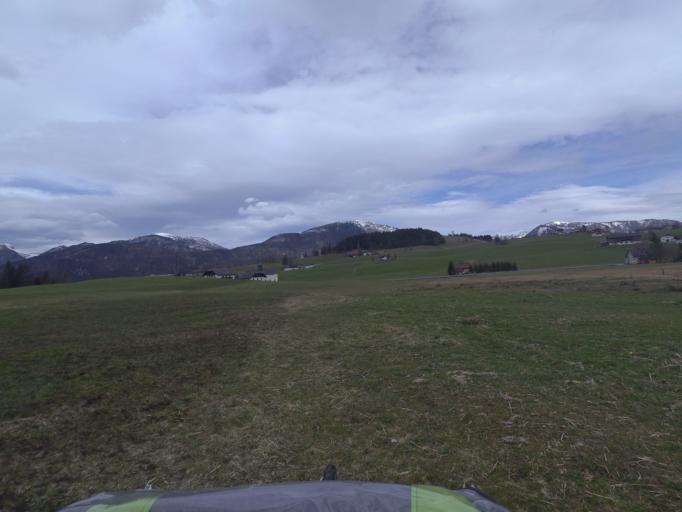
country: AT
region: Salzburg
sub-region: Politischer Bezirk Hallein
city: Abtenau
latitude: 47.5749
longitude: 13.3250
